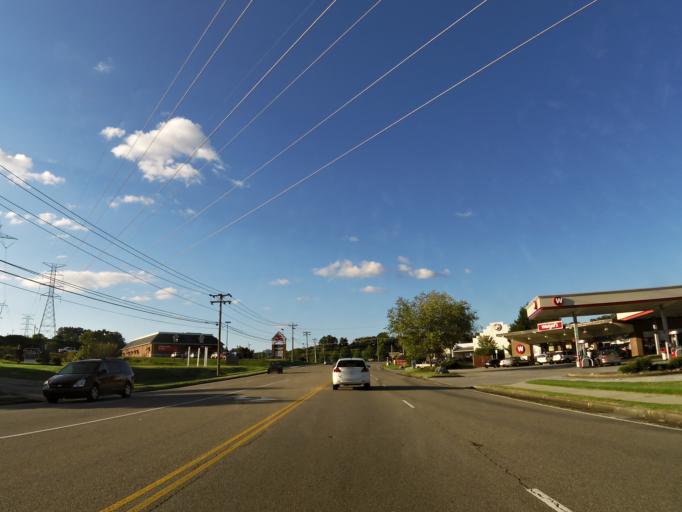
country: US
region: Tennessee
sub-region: Knox County
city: Farragut
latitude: 35.9393
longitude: -84.0946
